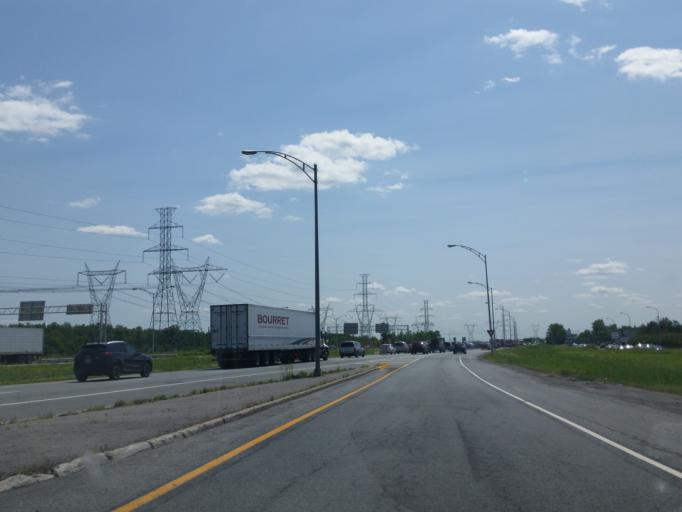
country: CA
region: Quebec
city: Saint-Bruno-de-Montarville
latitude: 45.4776
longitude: -73.3868
